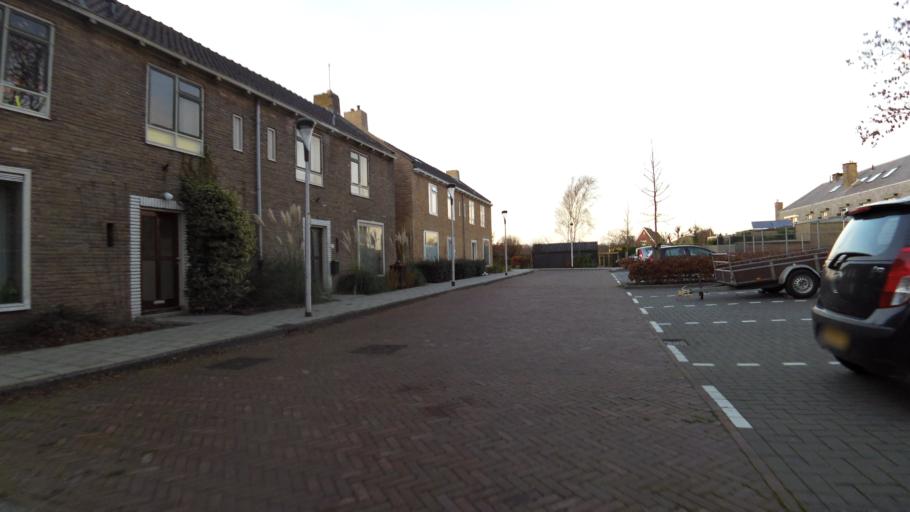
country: NL
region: South Holland
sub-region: Gemeente Noordwijkerhout
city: Noordwijkerhout
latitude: 52.2799
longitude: 4.4888
